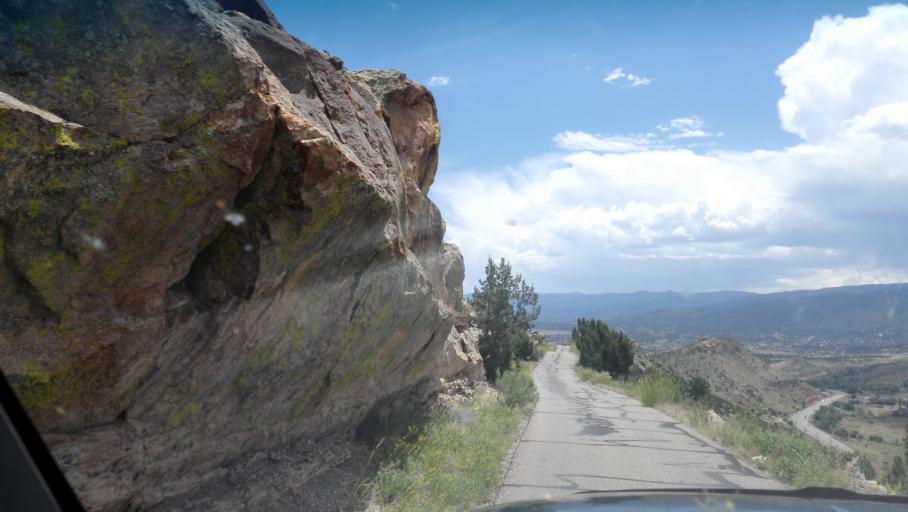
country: US
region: Colorado
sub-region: Fremont County
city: Canon City
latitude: 38.4586
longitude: -105.2507
